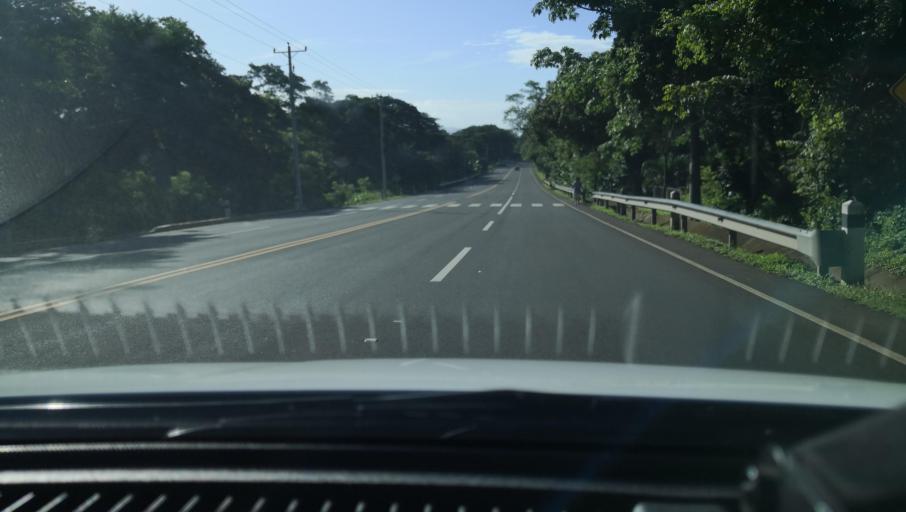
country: NI
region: Granada
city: Nandaime
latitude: 11.7890
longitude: -86.0626
